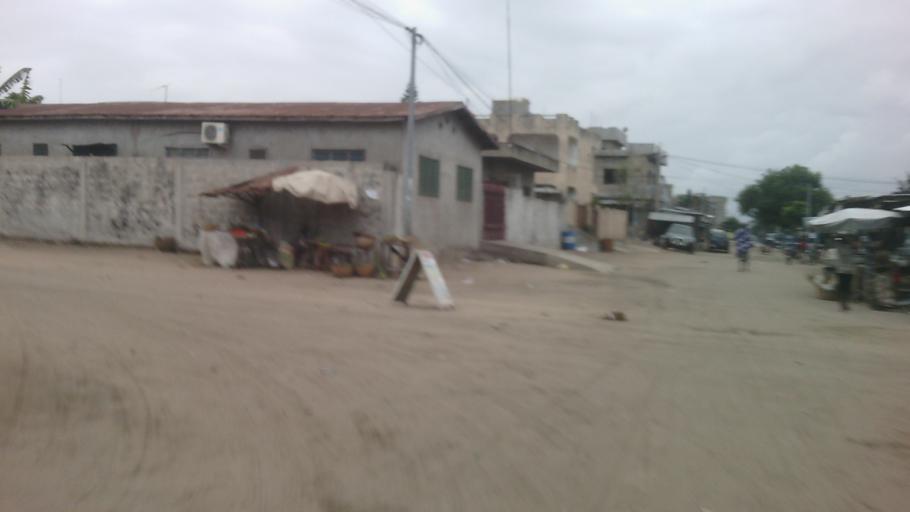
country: BJ
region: Atlantique
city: Abomey-Calavi
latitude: 6.3944
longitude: 2.3613
